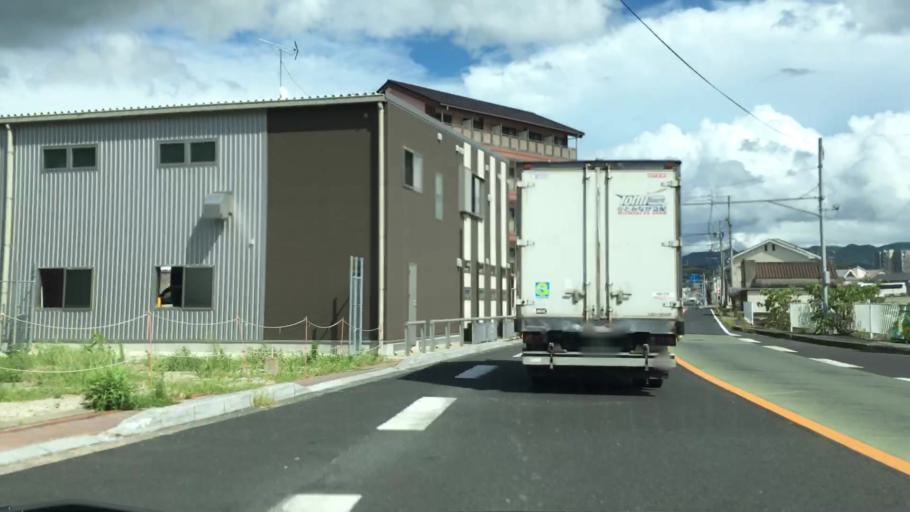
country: JP
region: Nagasaki
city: Sasebo
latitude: 33.1394
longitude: 129.7923
